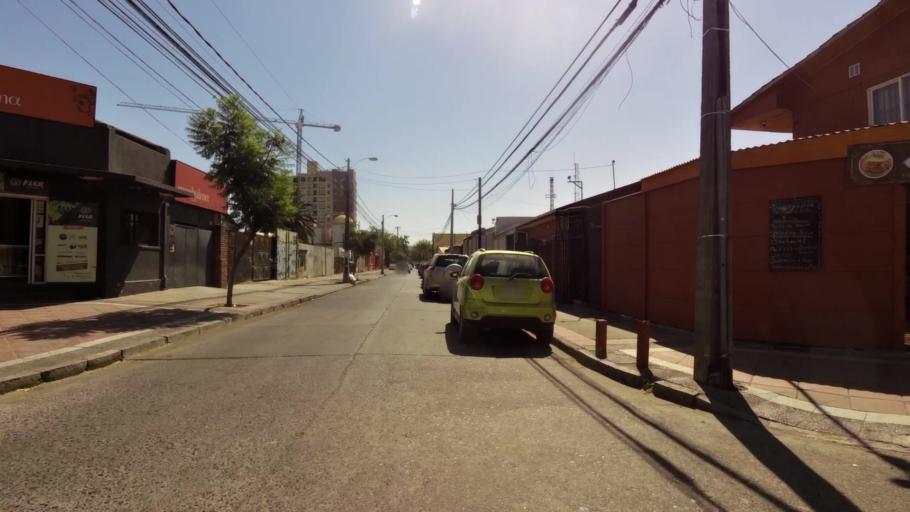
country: CL
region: Maule
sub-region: Provincia de Talca
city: Talca
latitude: -35.4299
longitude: -71.6586
